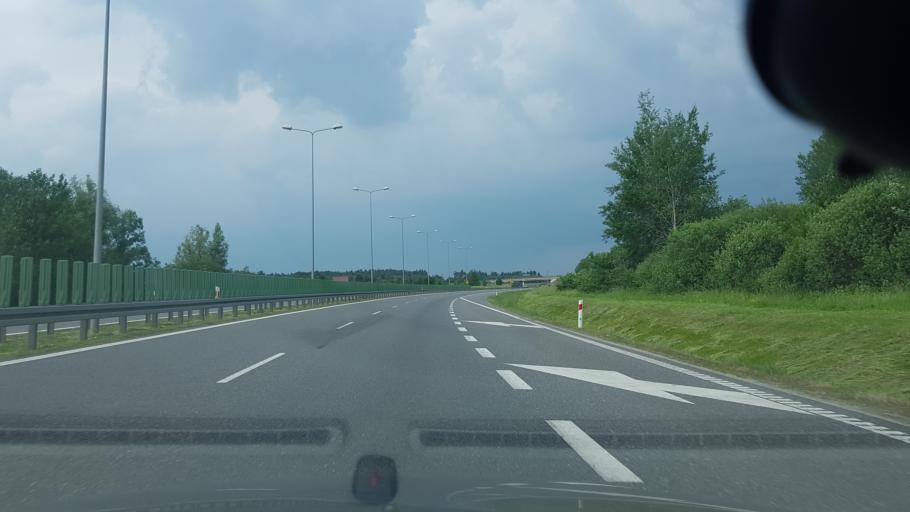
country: PL
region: Masovian Voivodeship
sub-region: Powiat legionowski
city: Serock
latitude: 52.5119
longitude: 21.0499
